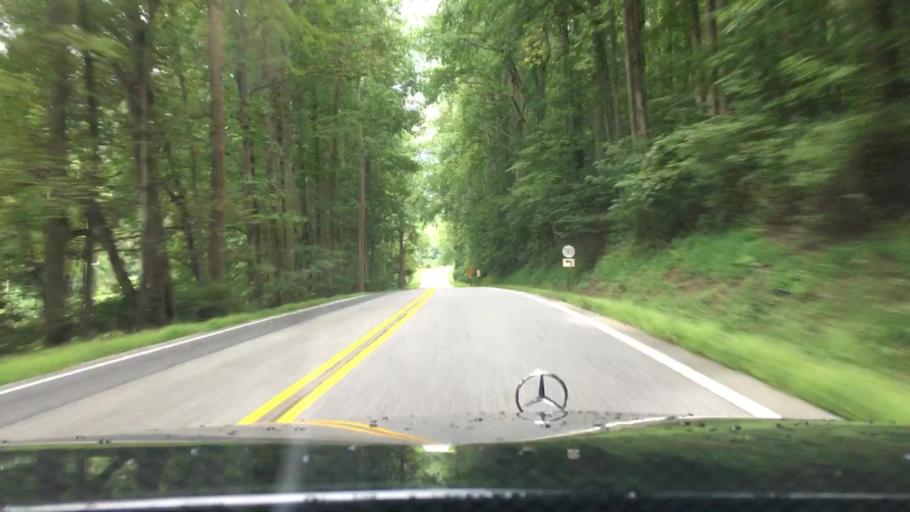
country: US
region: Virginia
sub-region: Nelson County
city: Nellysford
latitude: 37.8399
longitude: -78.9279
